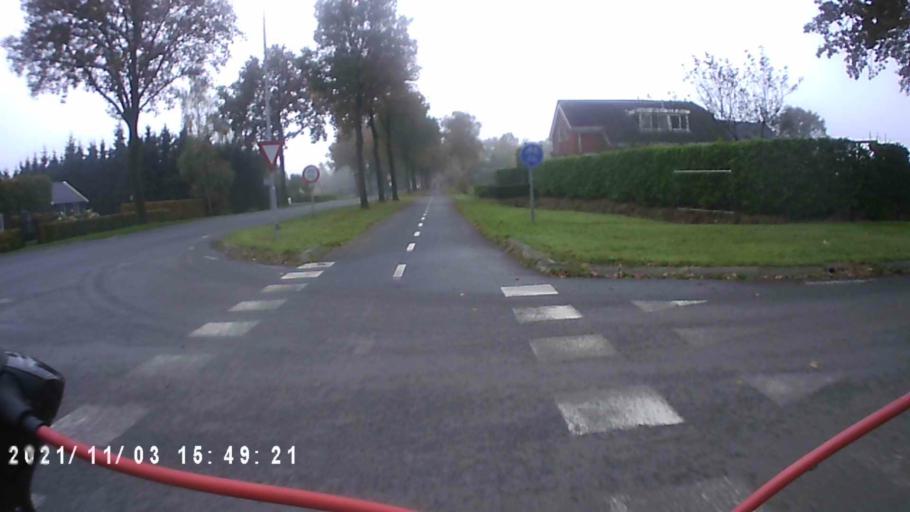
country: NL
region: Groningen
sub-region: Gemeente Leek
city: Leek
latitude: 53.0844
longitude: 6.3381
